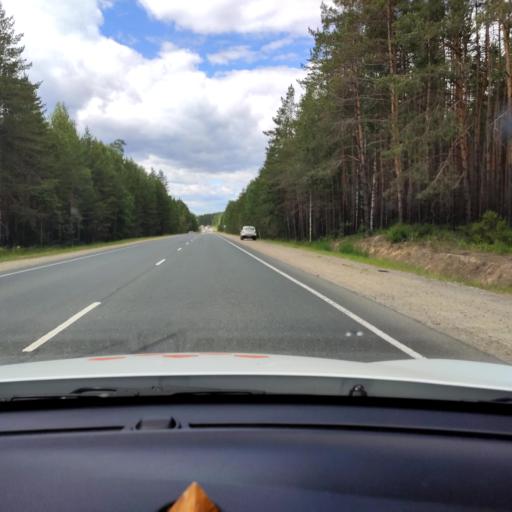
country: RU
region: Mariy-El
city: Pomary
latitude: 56.0515
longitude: 48.3743
